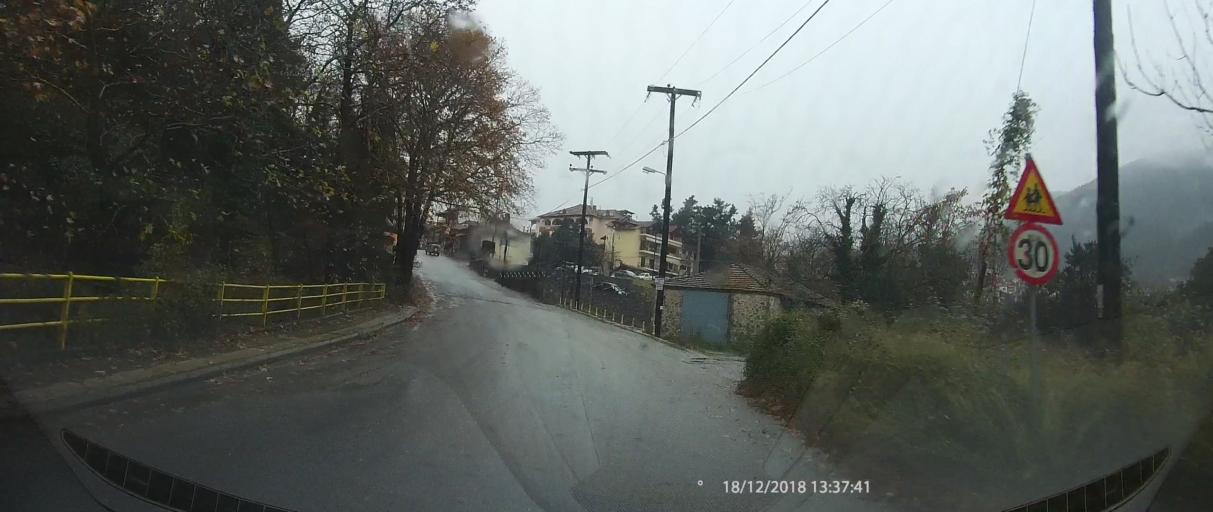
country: GR
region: Central Macedonia
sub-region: Nomos Pierias
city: Litochoro
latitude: 40.1065
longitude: 22.5022
